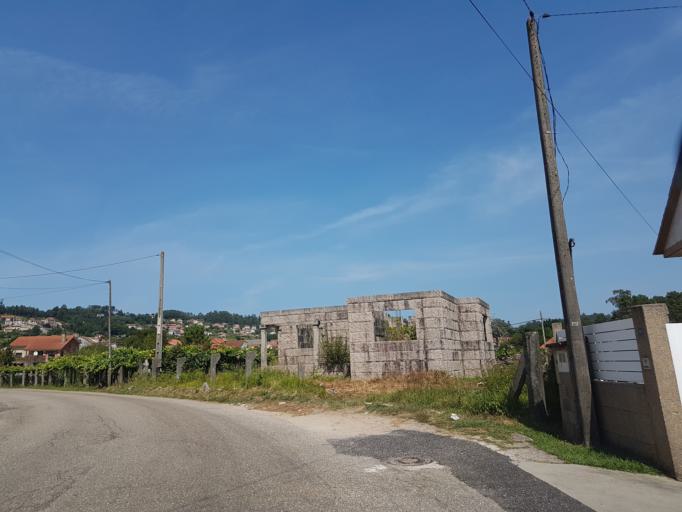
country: ES
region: Galicia
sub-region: Provincia de Pontevedra
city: Porrino
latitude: 42.2112
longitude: -8.6195
